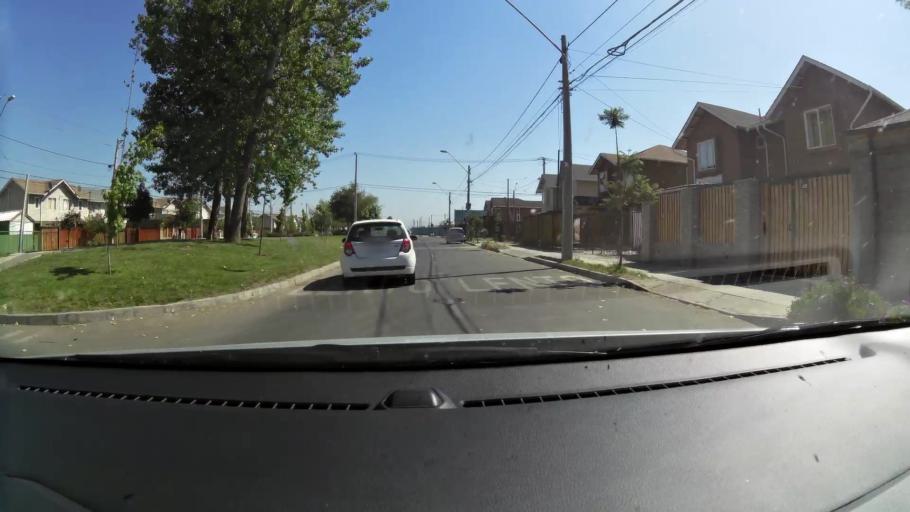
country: CL
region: Santiago Metropolitan
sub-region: Provincia de Maipo
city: San Bernardo
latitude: -33.6110
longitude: -70.6873
